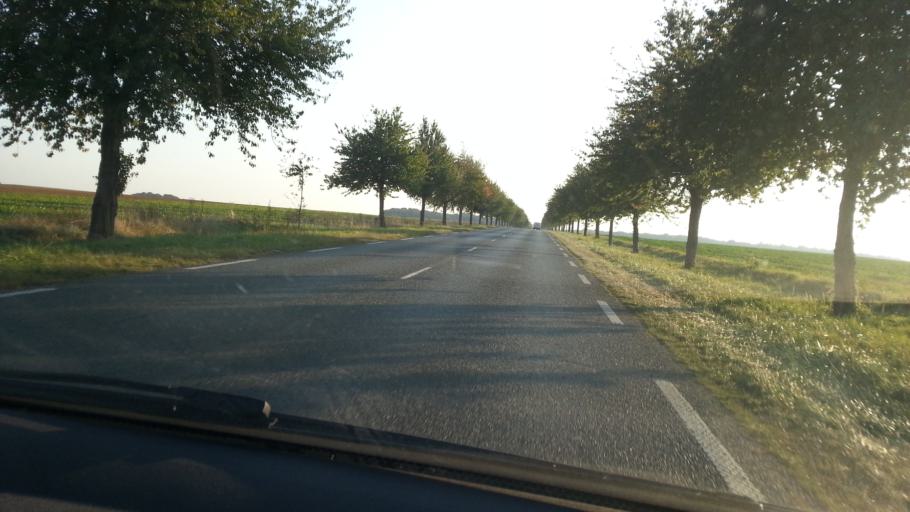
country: FR
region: Picardie
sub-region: Departement de l'Oise
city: Estrees-Saint-Denis
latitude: 49.4189
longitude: 2.6337
